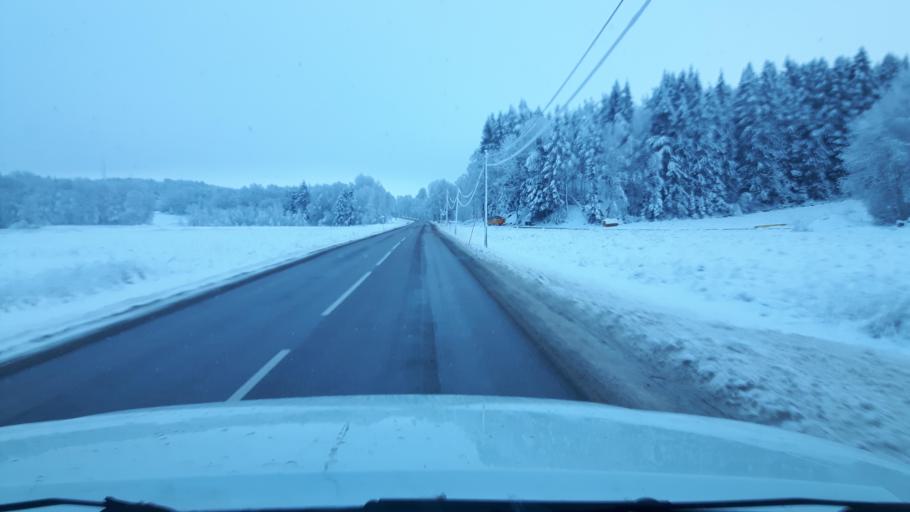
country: SE
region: Halland
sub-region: Kungsbacka Kommun
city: Fjaeras kyrkby
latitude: 57.4013
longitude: 12.2309
